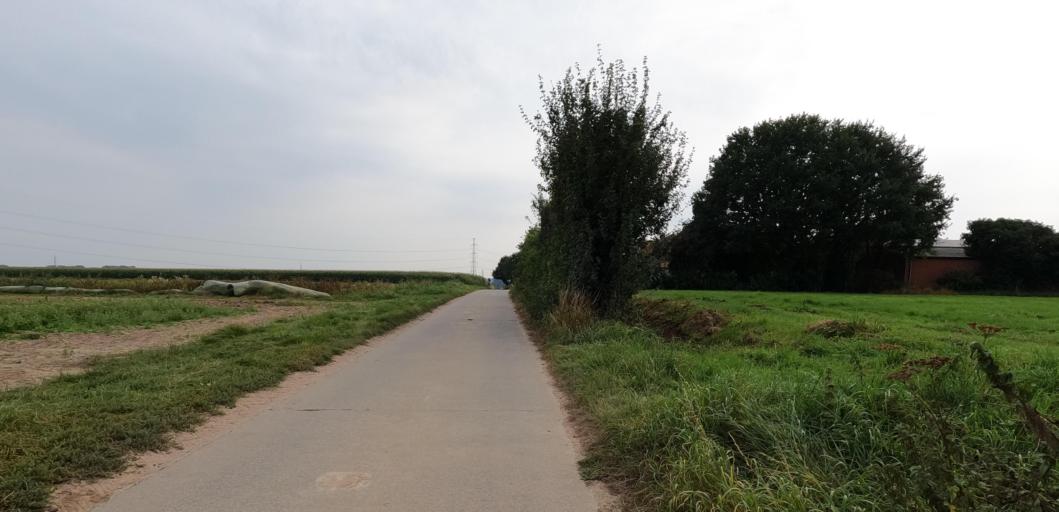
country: BE
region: Flanders
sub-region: Provincie Vlaams-Brabant
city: Merchtem
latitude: 50.9789
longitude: 4.2350
